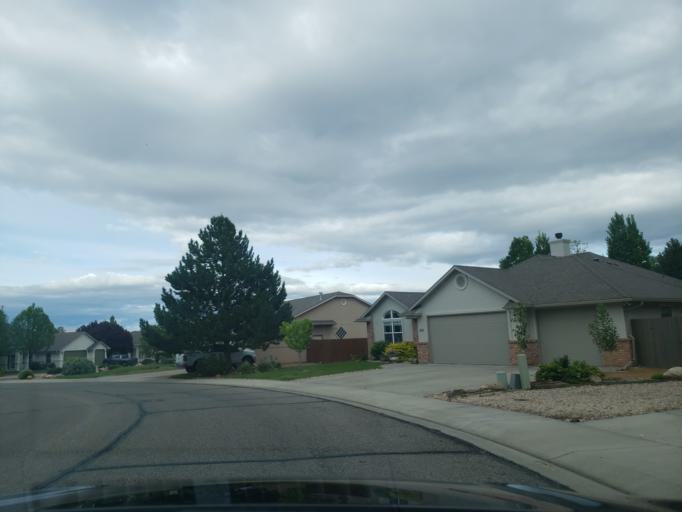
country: US
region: Colorado
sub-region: Mesa County
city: Redlands
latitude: 39.1029
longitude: -108.6675
